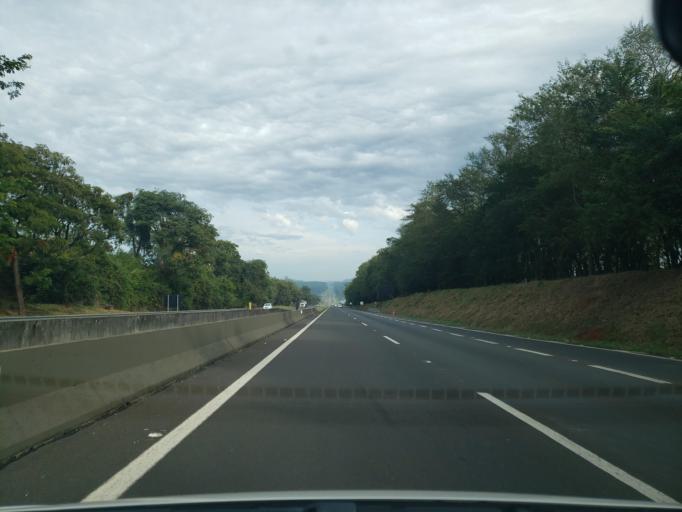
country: BR
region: Sao Paulo
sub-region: Itirapina
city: Itirapina
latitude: -22.2554
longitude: -47.8460
